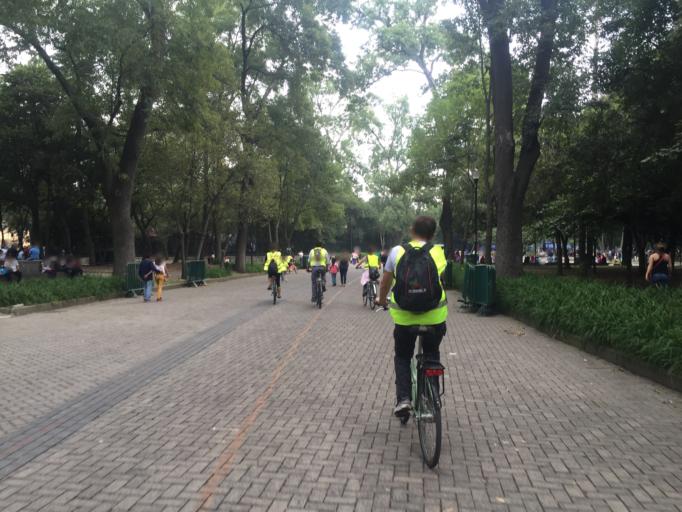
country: MX
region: Mexico City
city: Polanco
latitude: 19.4207
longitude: -99.1901
